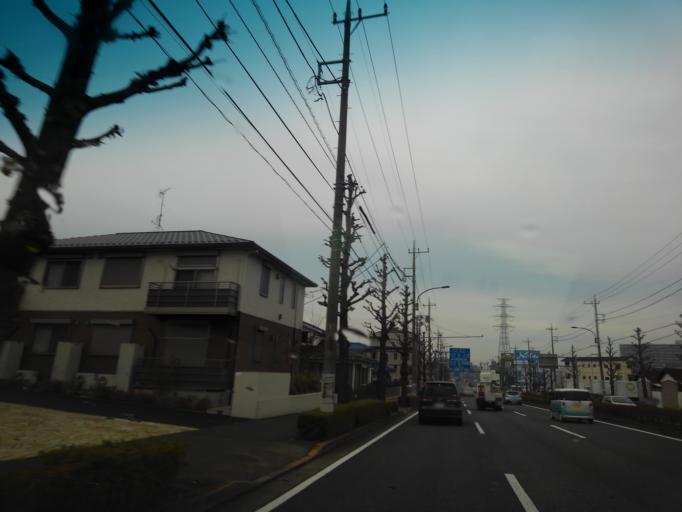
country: JP
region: Tokyo
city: Hino
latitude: 35.6413
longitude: 139.4510
